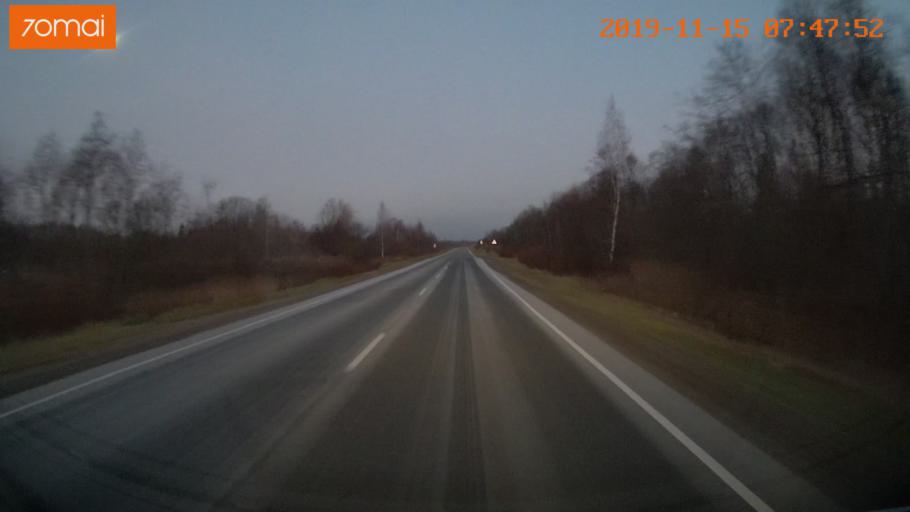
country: RU
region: Vologda
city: Sheksna
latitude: 58.8455
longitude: 38.2532
